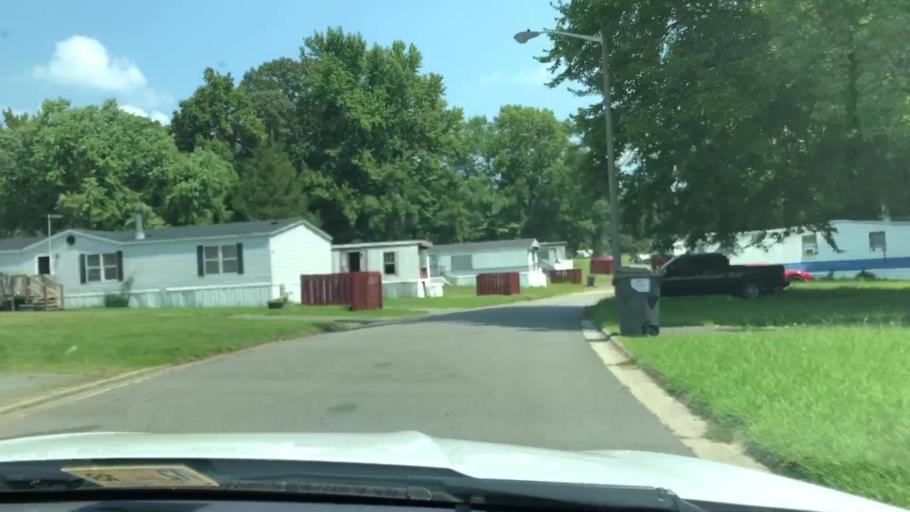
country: US
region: Virginia
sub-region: City of Williamsburg
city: Williamsburg
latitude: 37.2176
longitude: -76.6157
